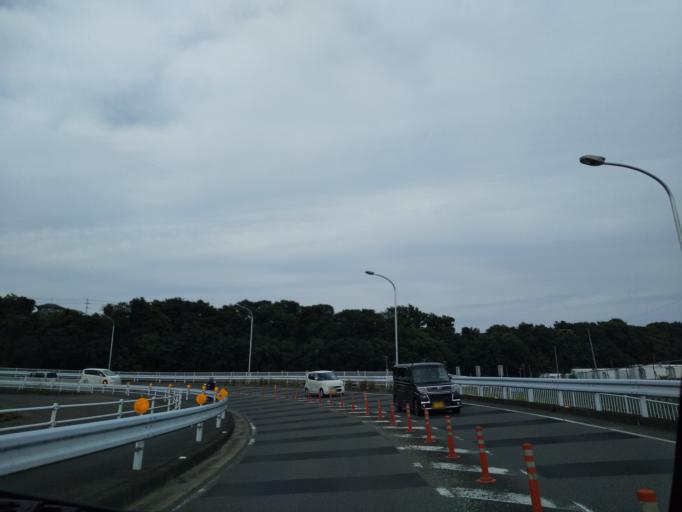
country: JP
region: Kanagawa
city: Zama
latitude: 35.4834
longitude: 139.3602
